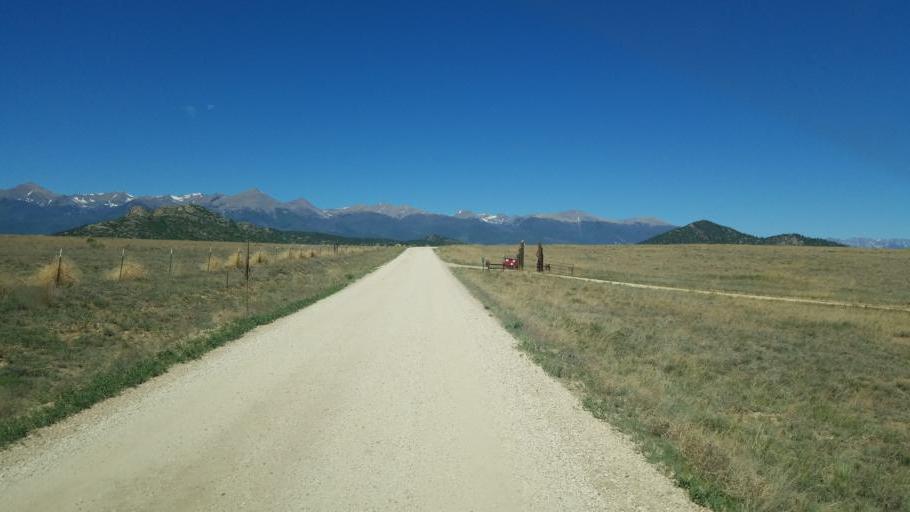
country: US
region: Colorado
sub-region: Custer County
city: Westcliffe
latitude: 38.2356
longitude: -105.4851
